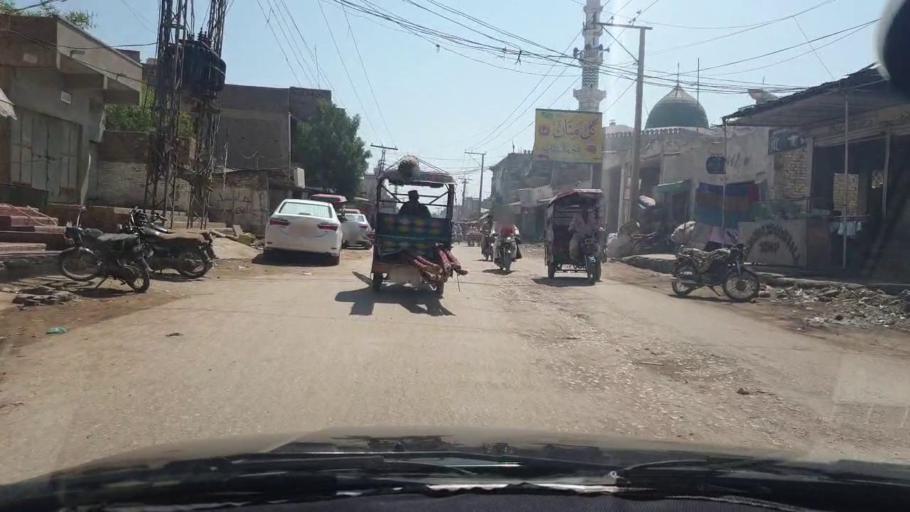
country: PK
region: Sindh
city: Tando Allahyar
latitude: 25.4573
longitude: 68.7189
